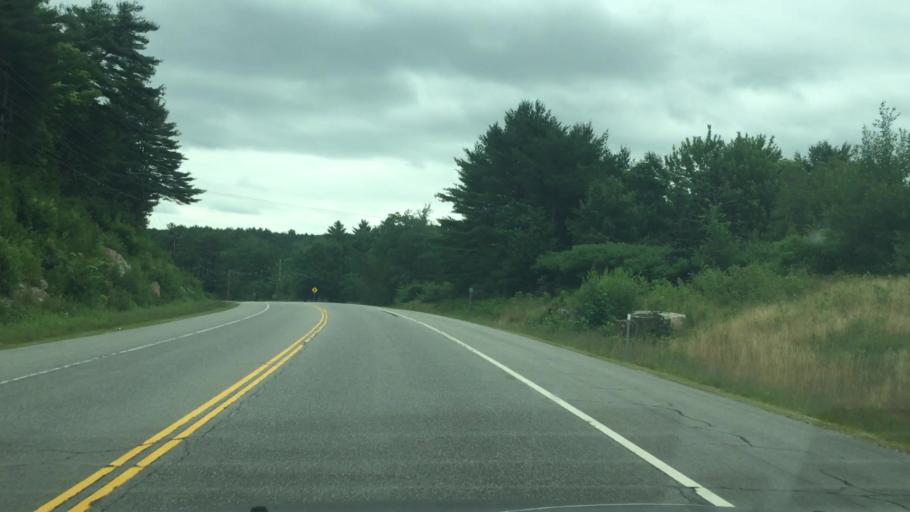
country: US
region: New Hampshire
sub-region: Belknap County
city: Meredith
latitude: 43.6227
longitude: -71.5458
